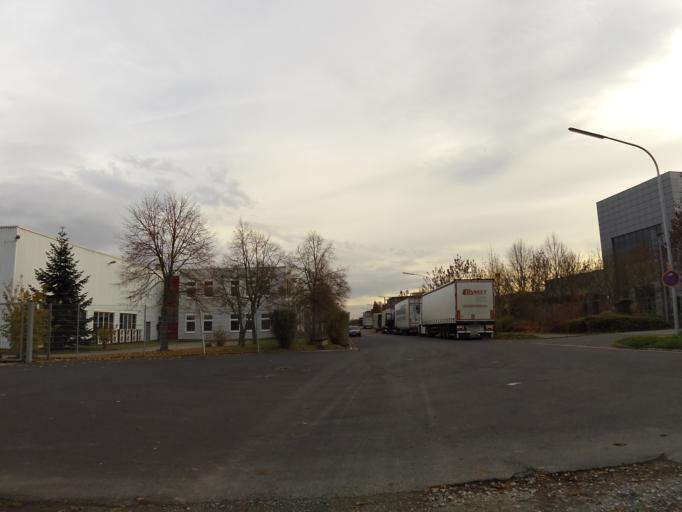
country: DE
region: Hesse
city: Morfelden-Walldorf
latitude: 49.9895
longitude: 8.5839
